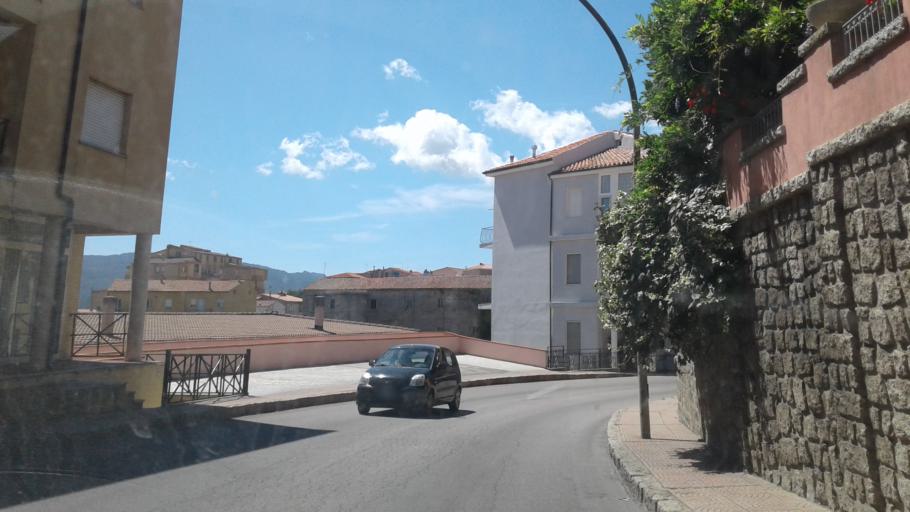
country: IT
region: Sardinia
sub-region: Provincia di Olbia-Tempio
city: Tempio Pausania
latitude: 40.9033
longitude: 9.1069
